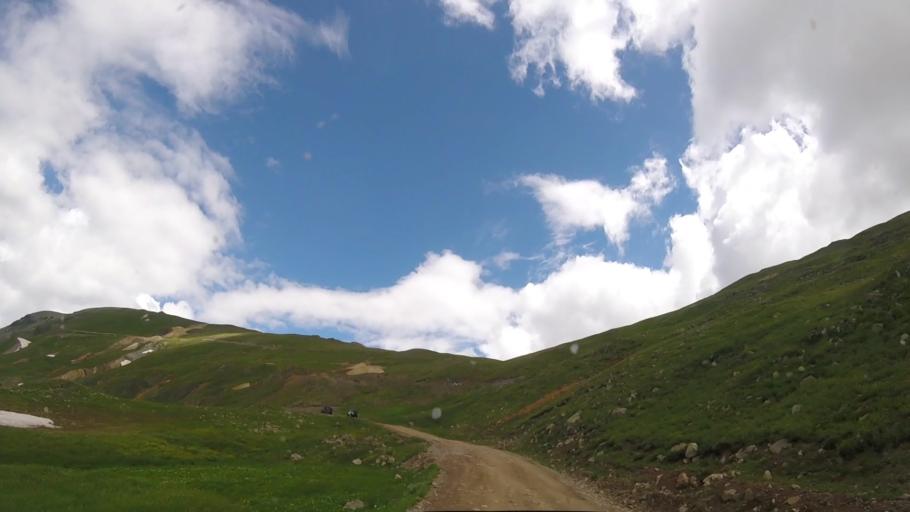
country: US
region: Colorado
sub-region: Ouray County
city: Ouray
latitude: 37.9594
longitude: -107.5757
